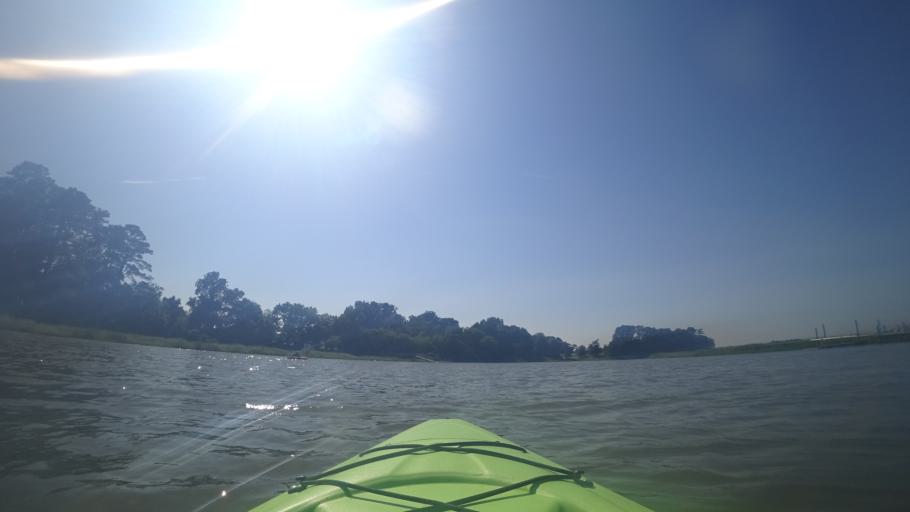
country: US
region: Virginia
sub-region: Isle of Wight County
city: Smithfield
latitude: 36.9747
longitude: -76.6206
